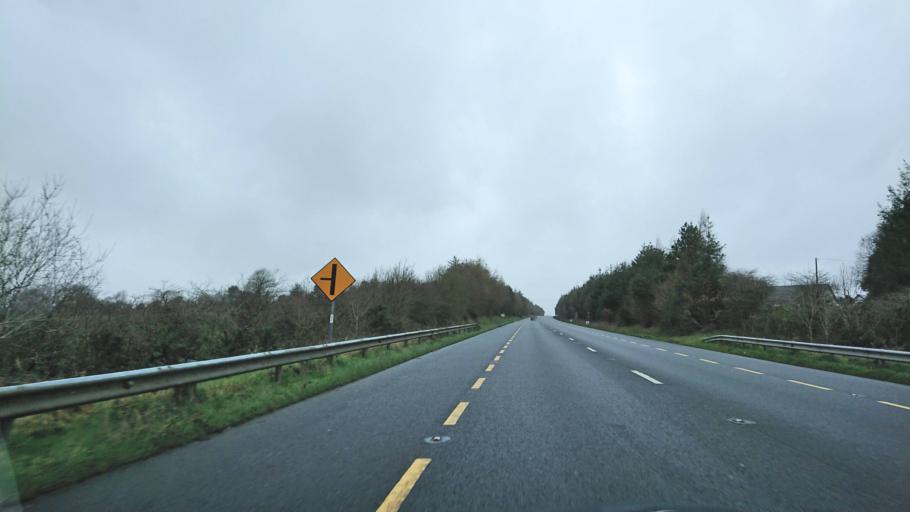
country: IE
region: Leinster
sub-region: Loch Garman
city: Enniscorthy
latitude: 52.3502
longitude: -6.6396
